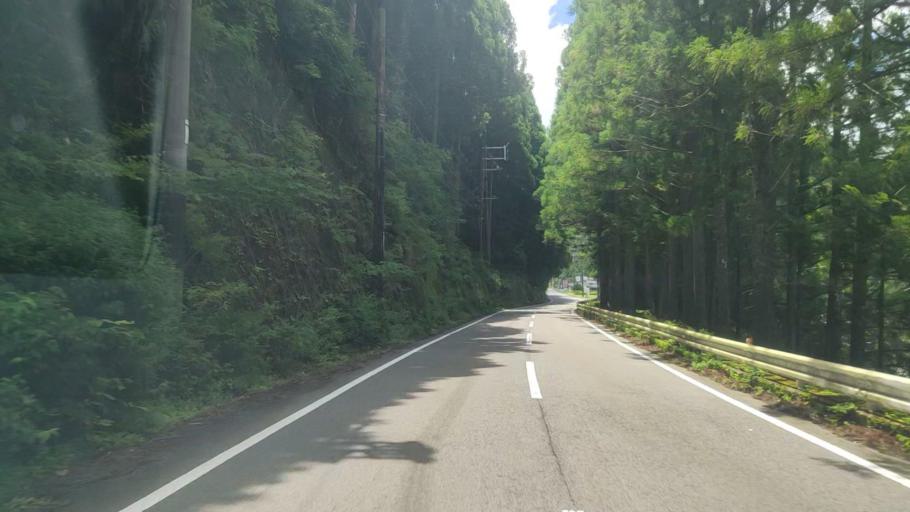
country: JP
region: Mie
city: Owase
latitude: 33.9673
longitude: 136.0613
